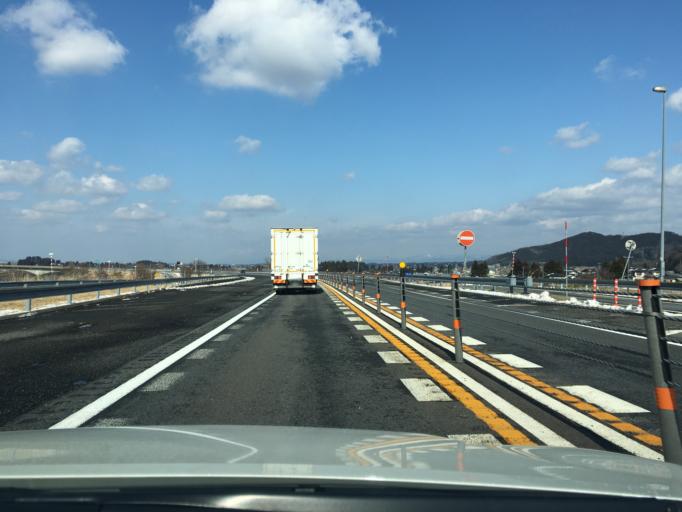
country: JP
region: Yamagata
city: Tsuruoka
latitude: 38.6162
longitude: 139.8430
